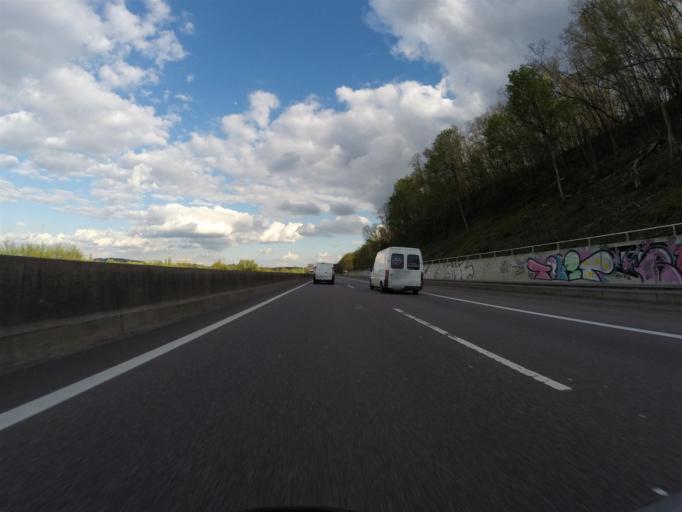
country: DE
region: Saarland
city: Wadgassen
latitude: 49.2812
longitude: 6.7687
